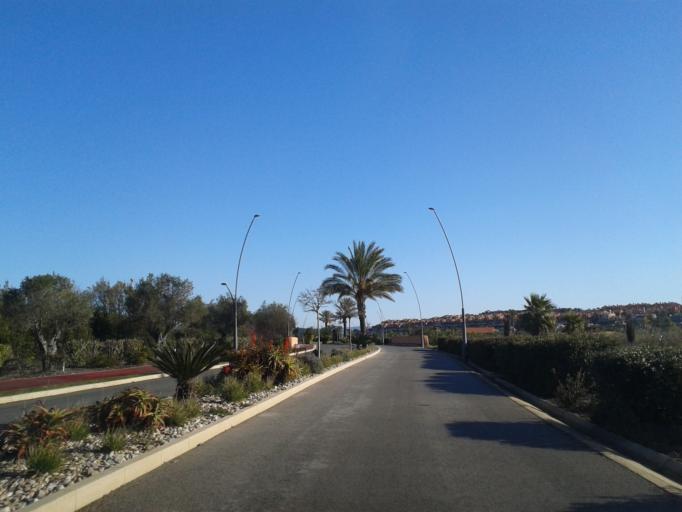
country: PT
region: Faro
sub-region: Silves
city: Armacao de Pera
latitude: 37.1488
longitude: -8.3658
